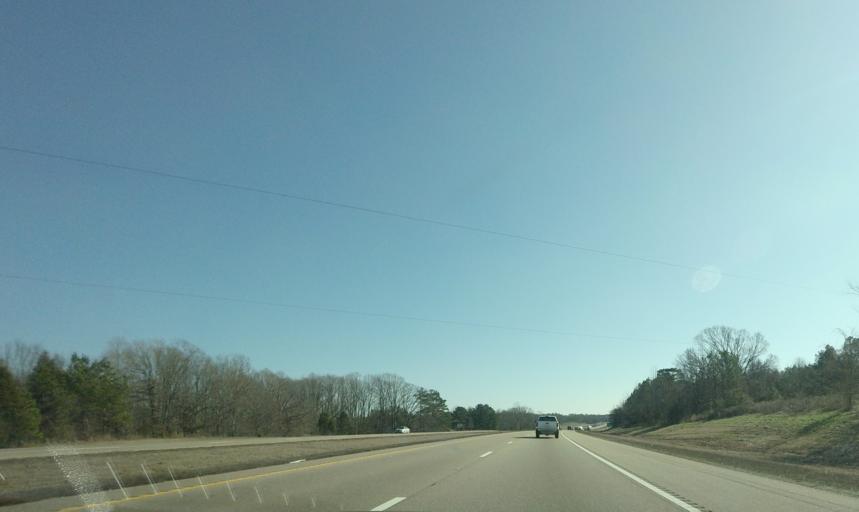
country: US
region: Mississippi
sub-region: Marshall County
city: Holly Springs
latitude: 34.8020
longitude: -89.4994
